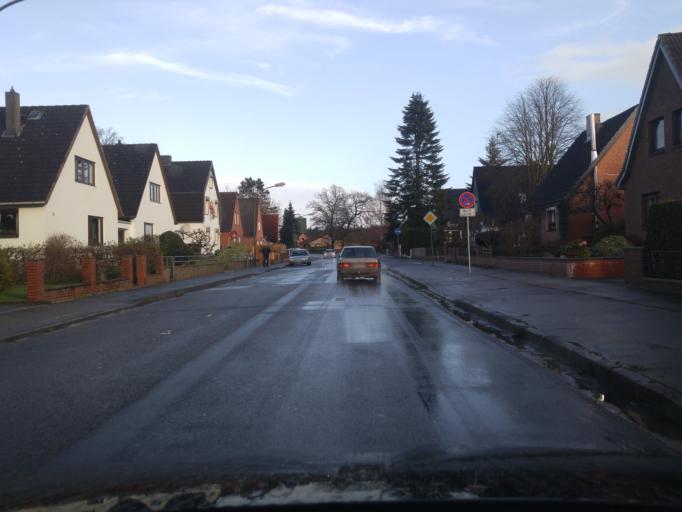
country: DE
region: Schleswig-Holstein
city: Ratekau
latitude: 53.9241
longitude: 10.7384
